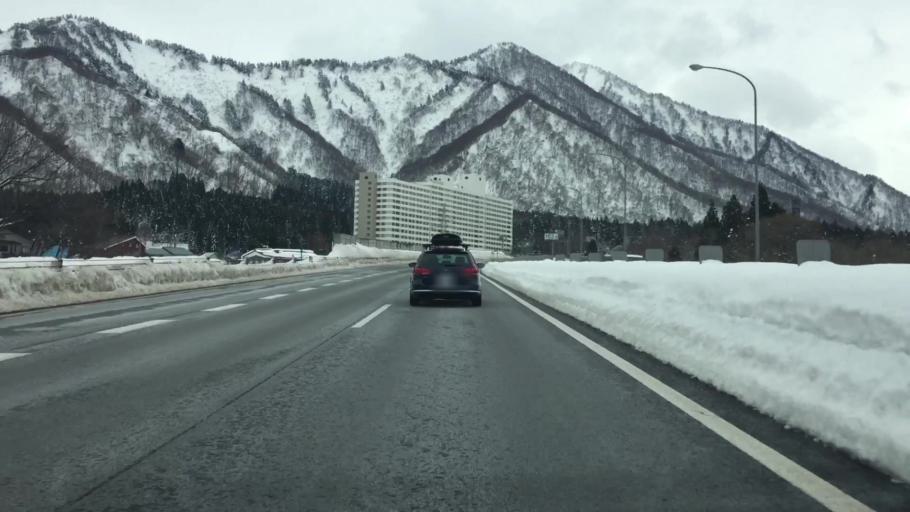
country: JP
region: Niigata
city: Shiozawa
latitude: 36.9072
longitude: 138.8439
